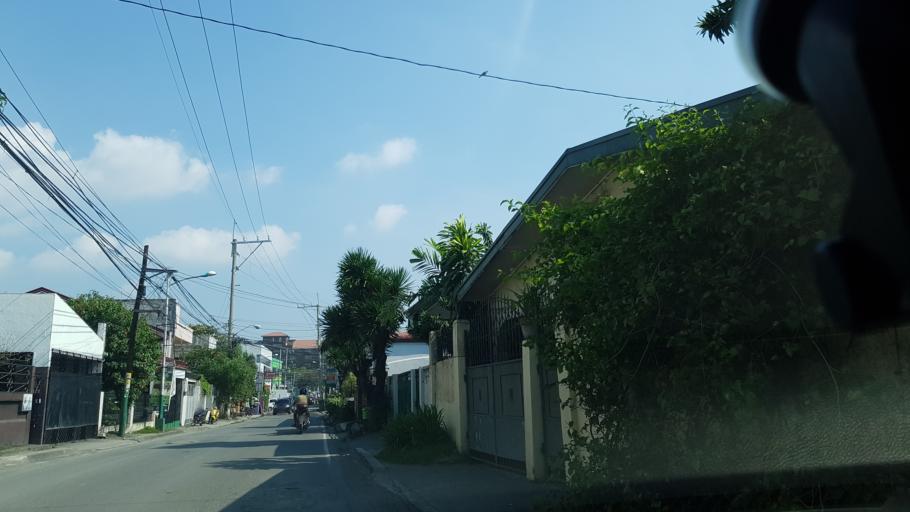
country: PH
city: Sambayanihan People's Village
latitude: 14.4986
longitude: 121.0124
